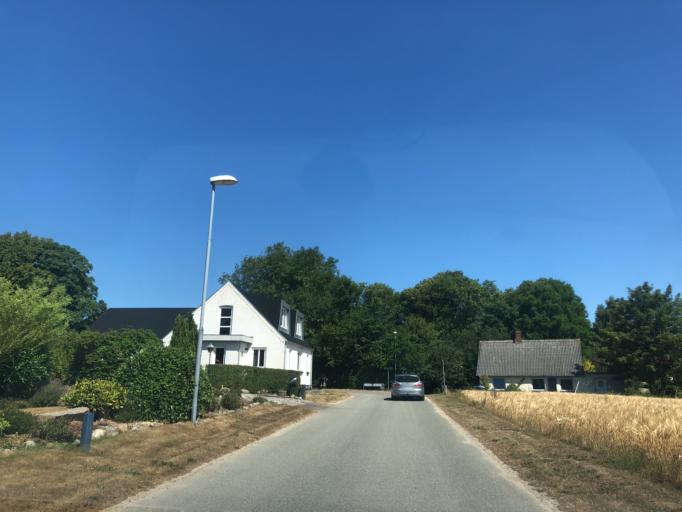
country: DK
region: North Denmark
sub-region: Morso Kommune
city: Nykobing Mors
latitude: 56.8240
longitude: 8.9962
